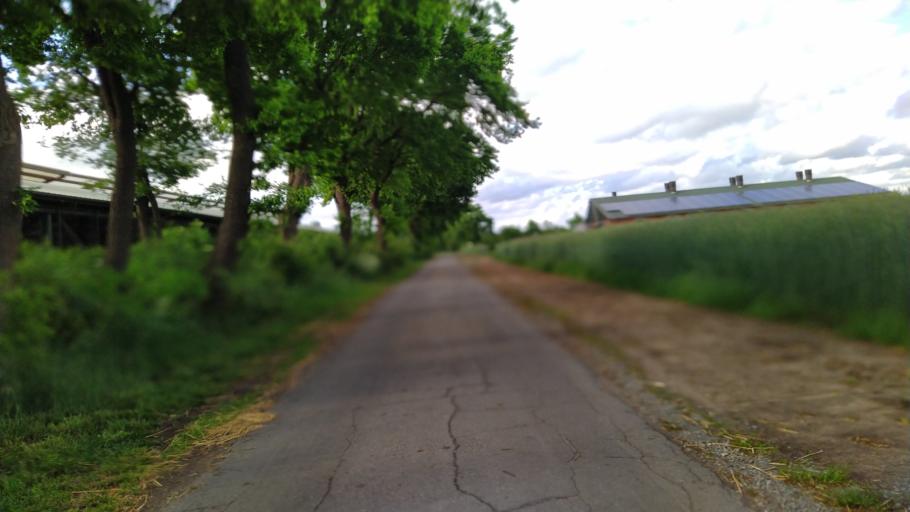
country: DE
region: Lower Saxony
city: Kutenholz
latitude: 53.4629
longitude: 9.3118
